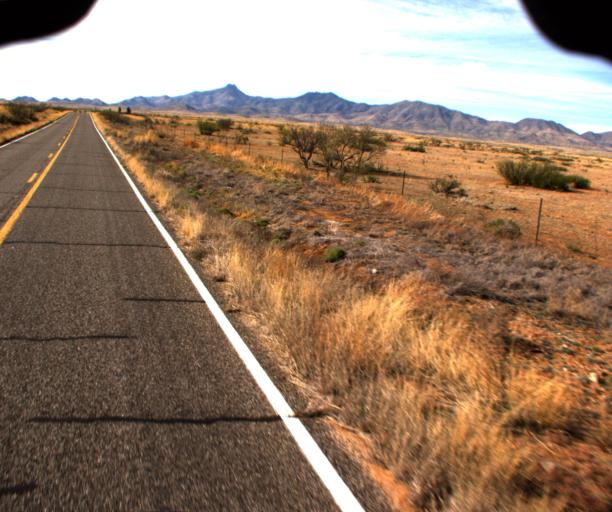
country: US
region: Arizona
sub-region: Cochise County
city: Willcox
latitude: 32.0889
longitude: -109.5295
